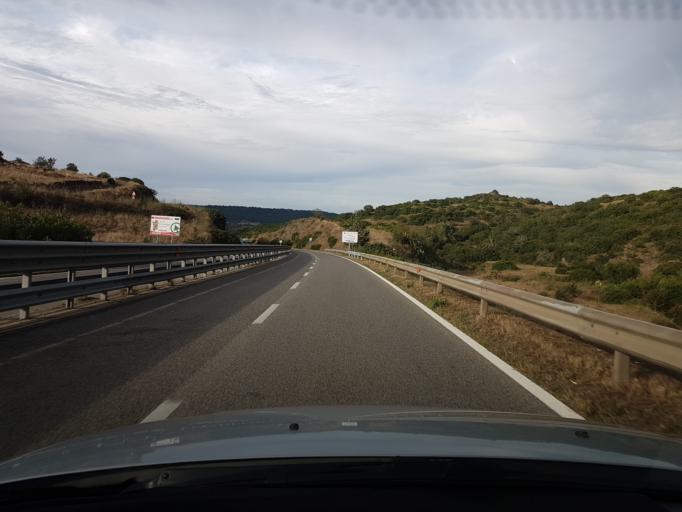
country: IT
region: Sardinia
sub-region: Provincia di Oristano
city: Soddi
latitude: 40.1337
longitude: 8.8663
